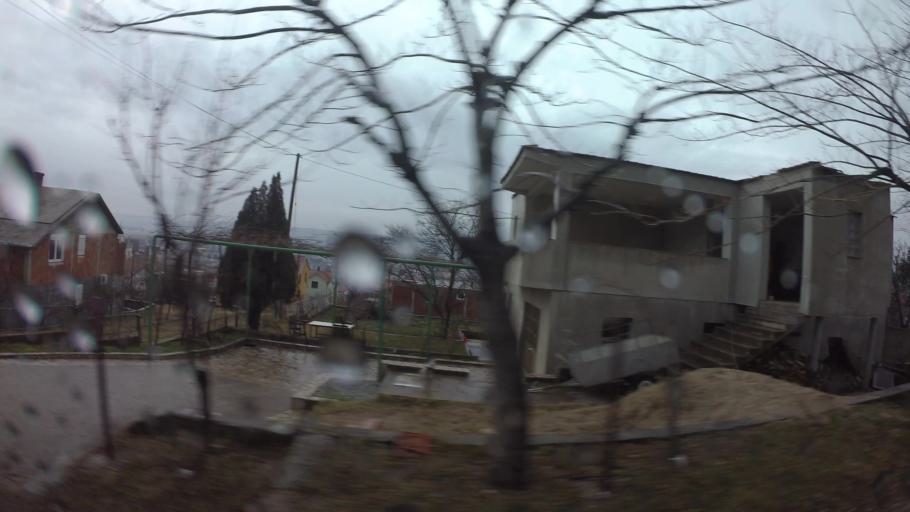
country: BA
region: Federation of Bosnia and Herzegovina
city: Rodoc
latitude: 43.3114
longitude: 17.8393
